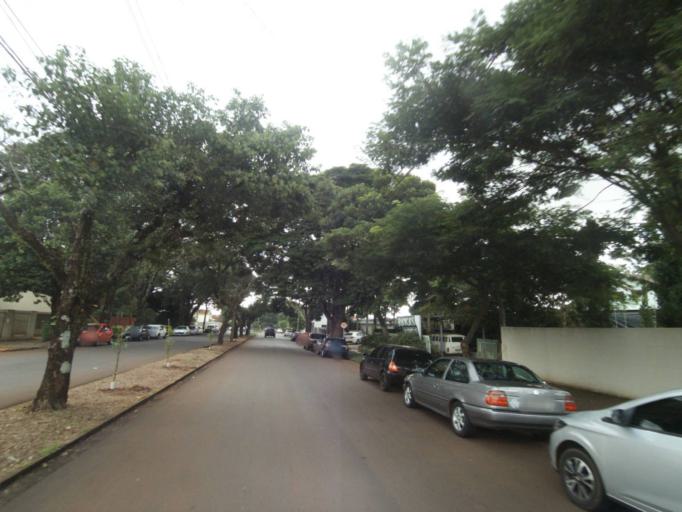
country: BR
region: Parana
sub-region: Campo Mourao
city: Campo Mourao
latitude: -24.0466
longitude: -52.3737
